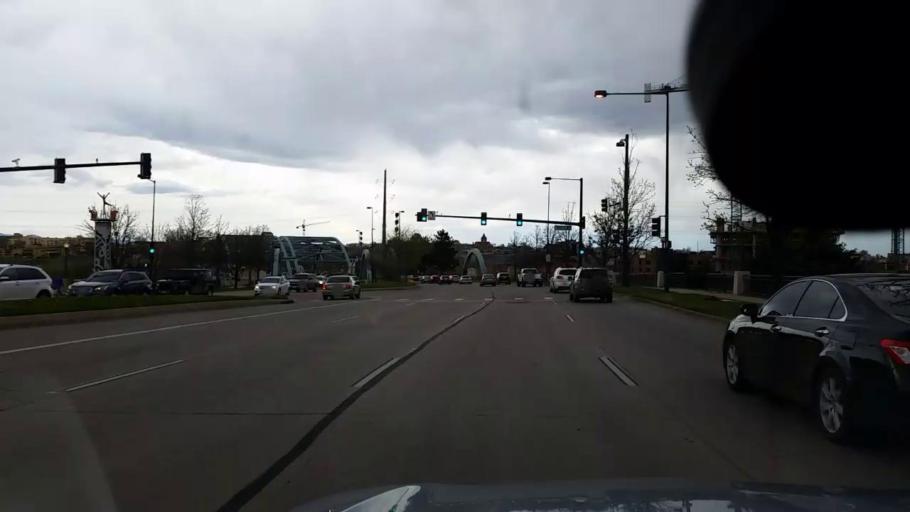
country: US
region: Colorado
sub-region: Denver County
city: Denver
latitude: 39.7521
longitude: -105.0070
